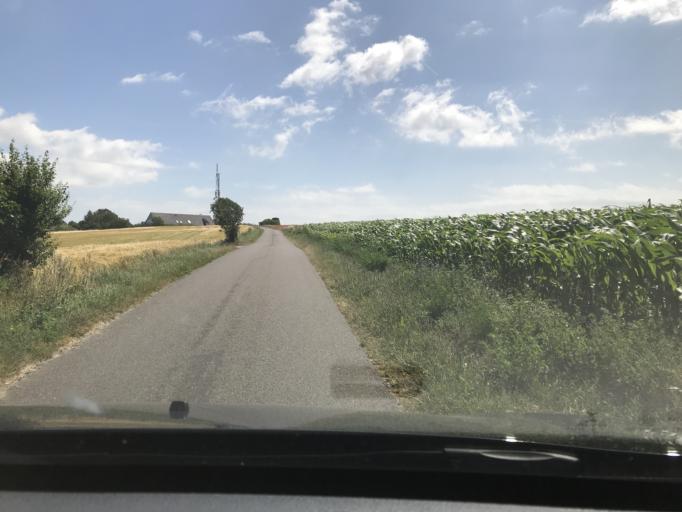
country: DK
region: South Denmark
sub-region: AEro Kommune
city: AEroskobing
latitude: 54.9033
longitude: 10.3055
